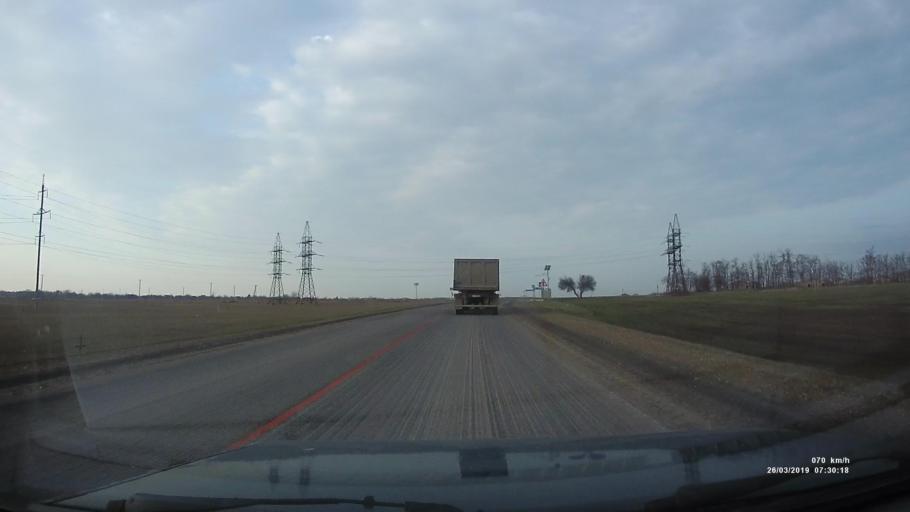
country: RU
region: Rostov
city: Novobessergenovka
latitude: 47.2376
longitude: 38.8081
